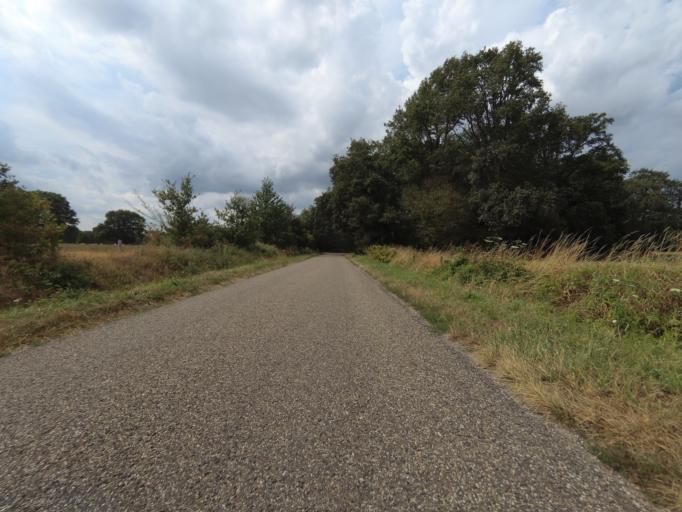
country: NL
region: Overijssel
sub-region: Gemeente Hof van Twente
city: Delden
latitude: 52.2390
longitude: 6.7507
